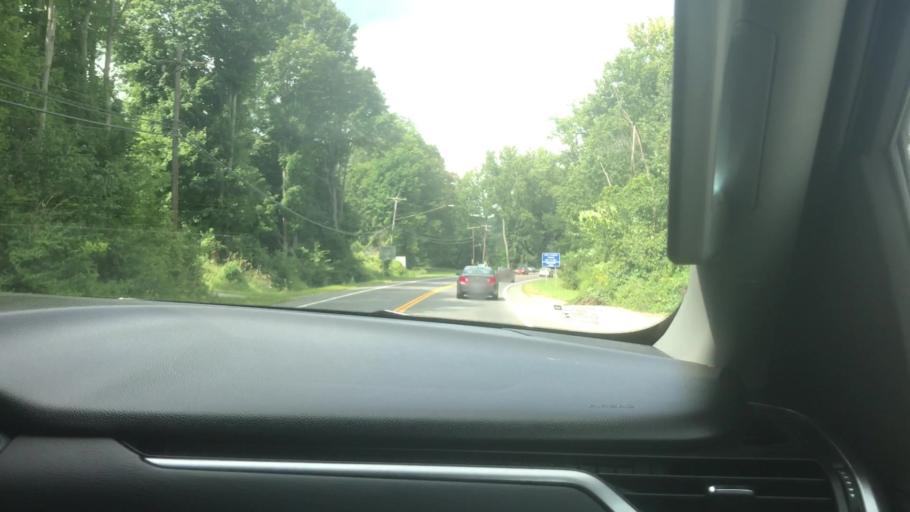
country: US
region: New York
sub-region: Dutchess County
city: Dover Plains
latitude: 41.8566
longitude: -73.5537
